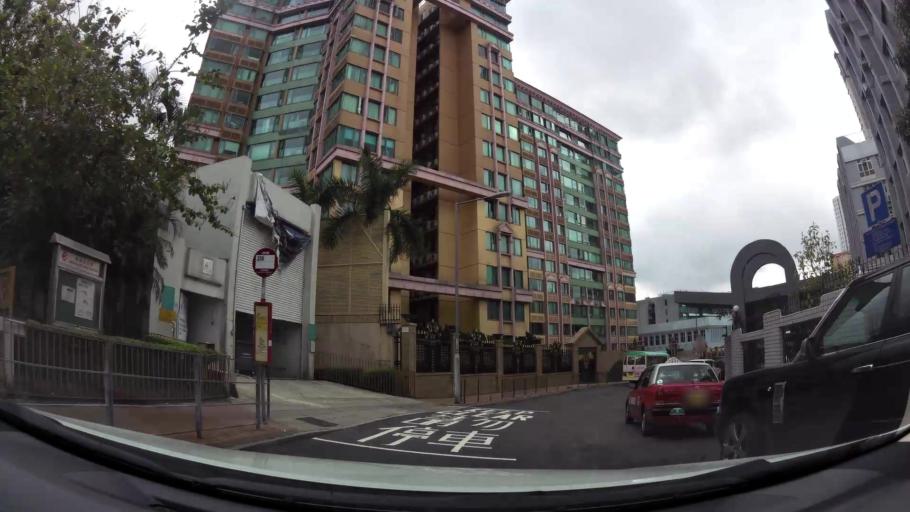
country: HK
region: Wong Tai Sin
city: Wong Tai Sin
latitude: 22.3433
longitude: 114.1825
